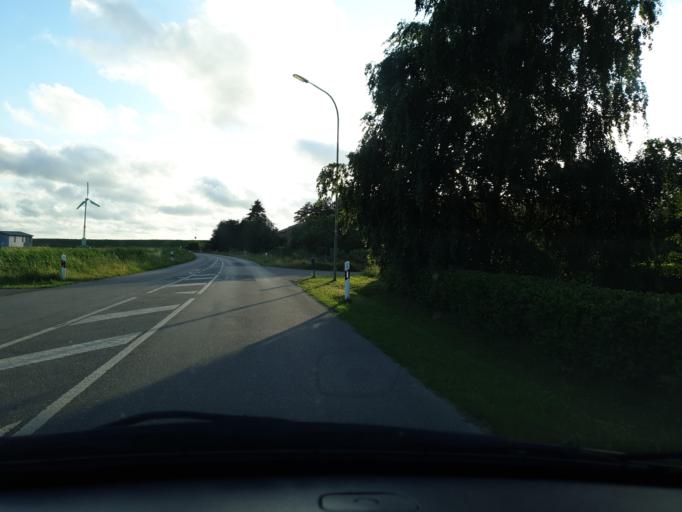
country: DE
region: Schleswig-Holstein
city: Busenwurth
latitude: 54.0586
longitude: 9.0197
